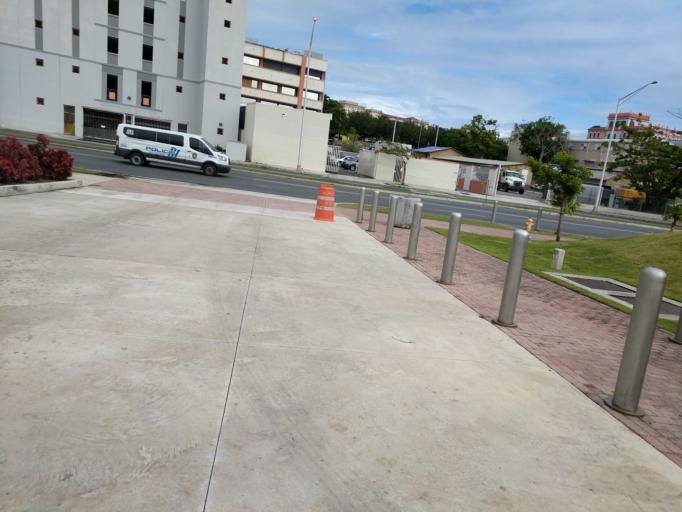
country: PR
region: San Juan
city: San Juan
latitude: 18.4646
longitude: -66.1050
